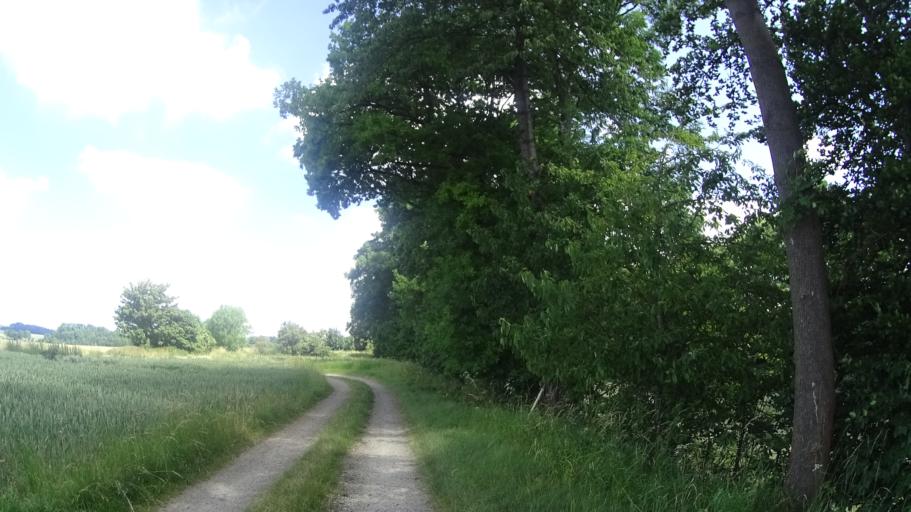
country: DE
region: Lower Saxony
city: Algermissen
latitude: 52.2443
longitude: 9.9489
